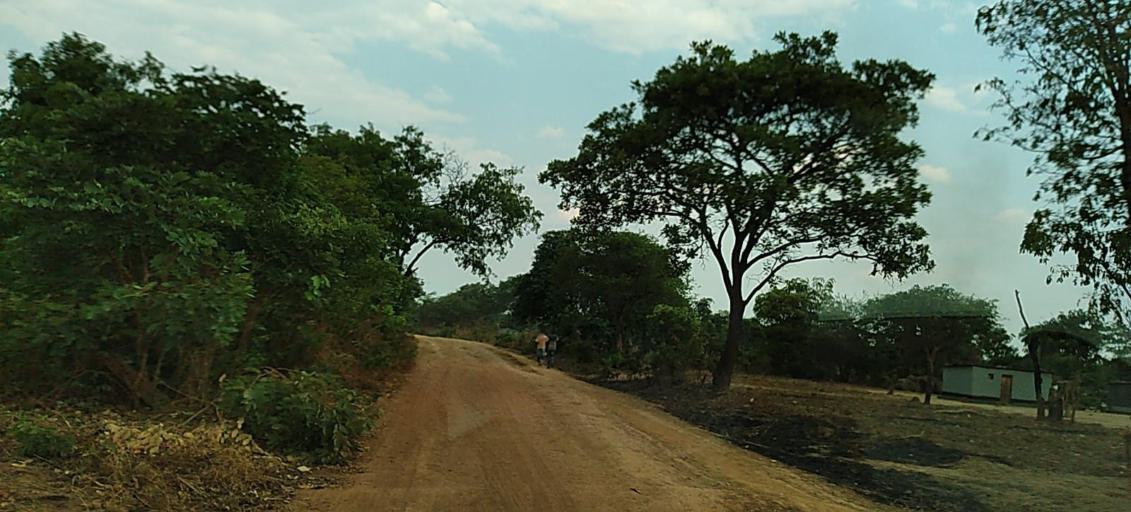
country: ZM
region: Copperbelt
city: Kalulushi
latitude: -13.0185
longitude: 27.9152
